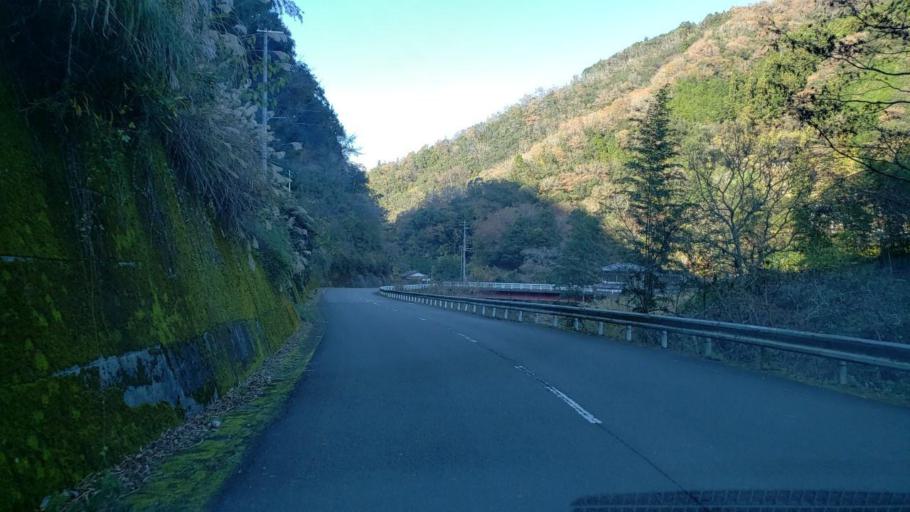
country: JP
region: Tokushima
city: Wakimachi
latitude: 34.0042
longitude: 134.0349
